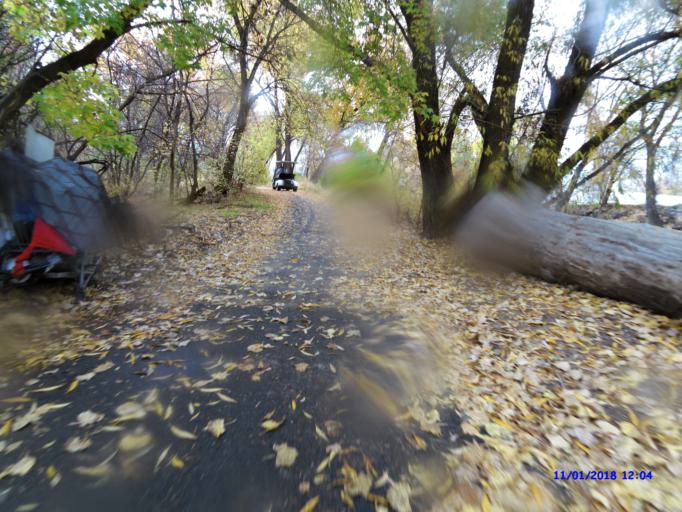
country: US
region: Utah
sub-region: Weber County
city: Ogden
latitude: 41.2281
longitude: -111.9978
